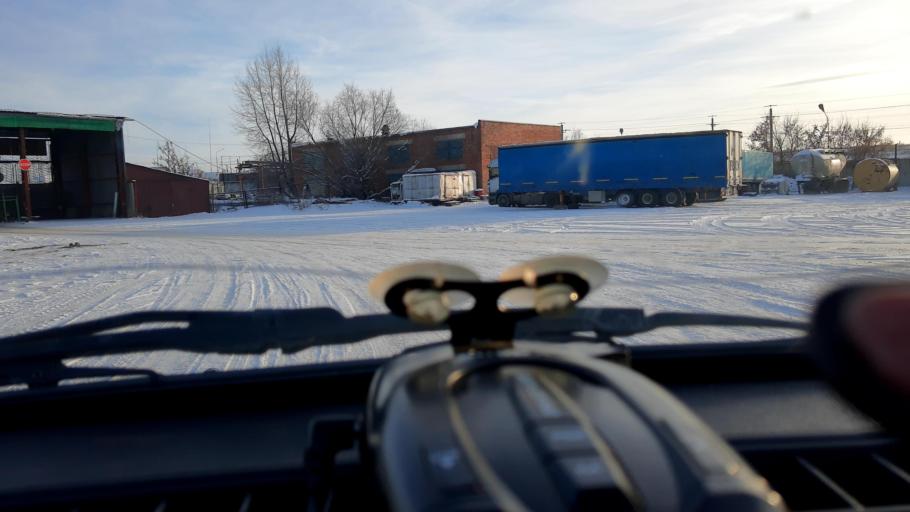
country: RU
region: Bashkortostan
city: Avdon
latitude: 54.6072
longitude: 55.8436
